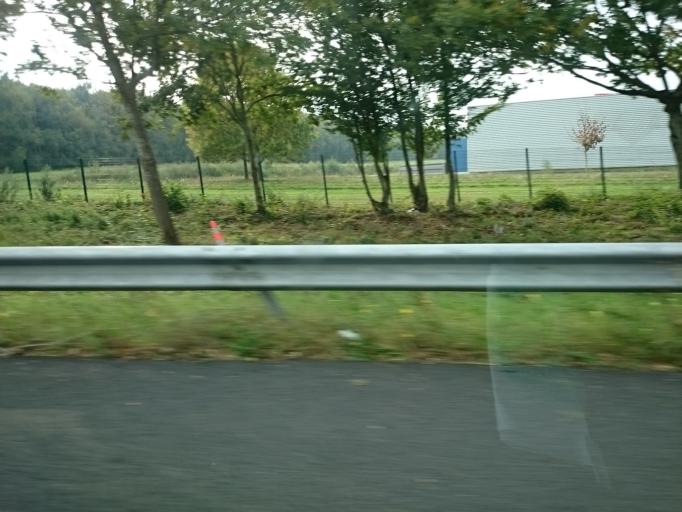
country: FR
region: Pays de la Loire
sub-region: Departement de la Loire-Atlantique
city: Derval
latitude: 47.6377
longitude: -1.6526
